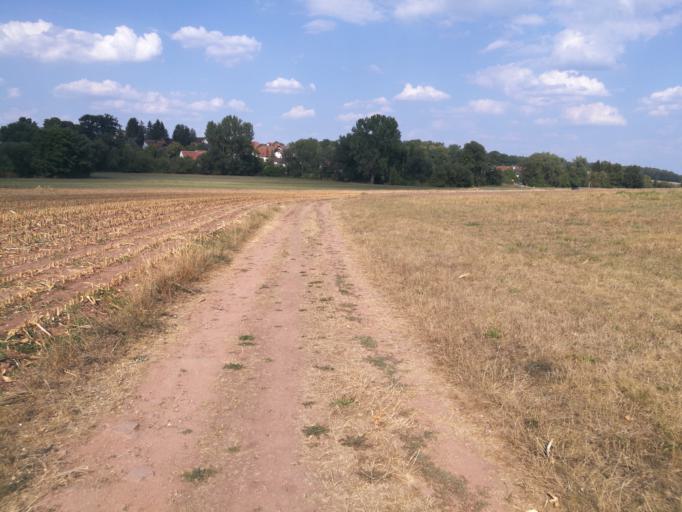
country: DE
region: Bavaria
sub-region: Regierungsbezirk Mittelfranken
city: Veitsbronn
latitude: 49.5067
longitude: 10.8969
